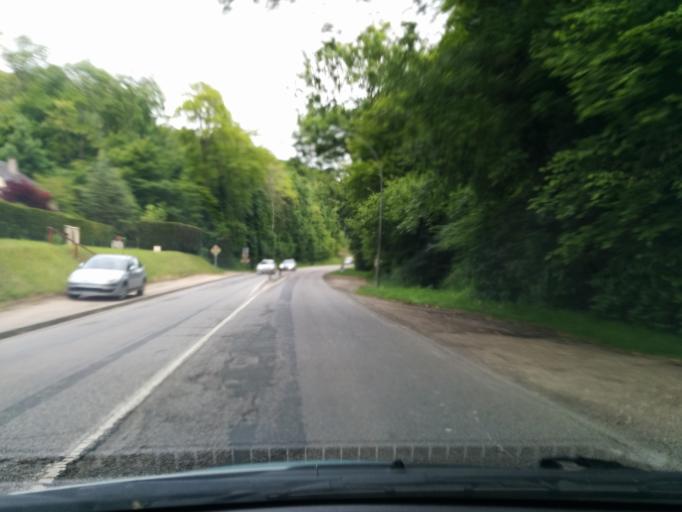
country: FR
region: Haute-Normandie
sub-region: Departement de l'Eure
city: Vernon
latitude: 49.1079
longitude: 1.4880
